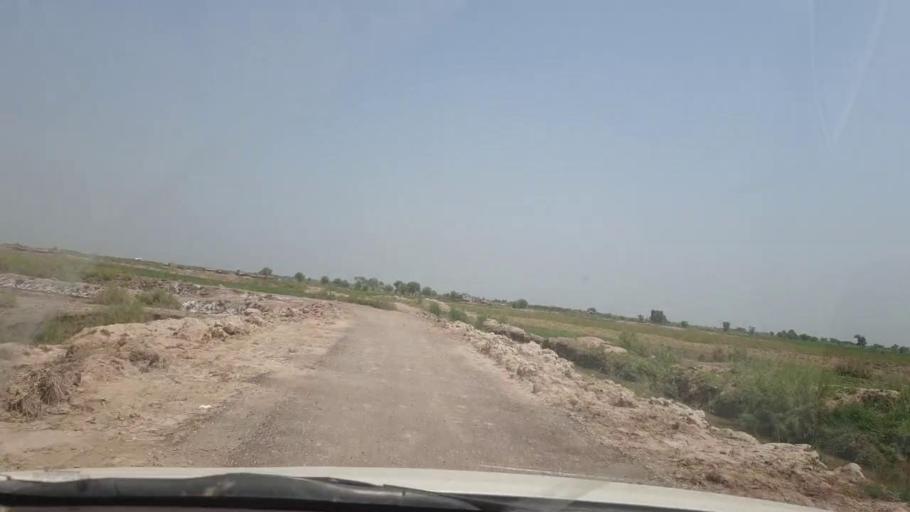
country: PK
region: Sindh
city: Lakhi
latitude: 27.8871
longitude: 68.7469
